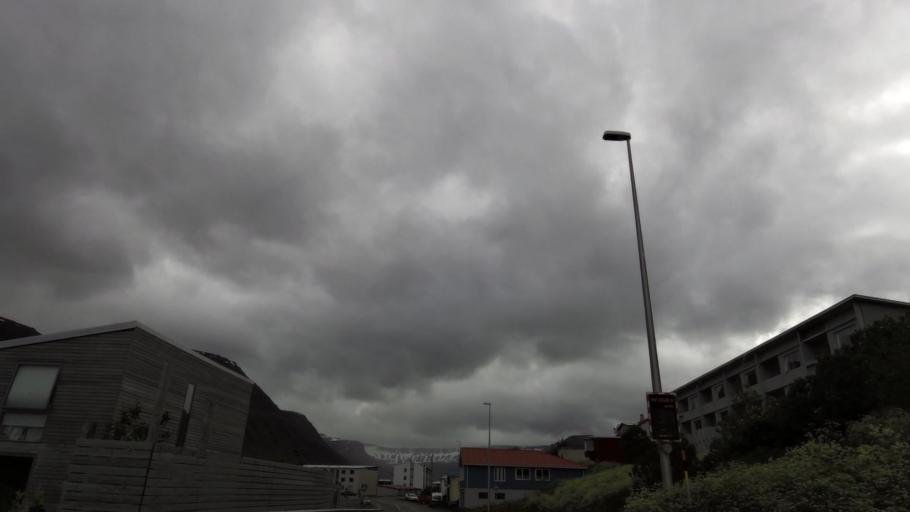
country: IS
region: Westfjords
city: Isafjoerdur
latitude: 66.0796
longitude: -23.1247
